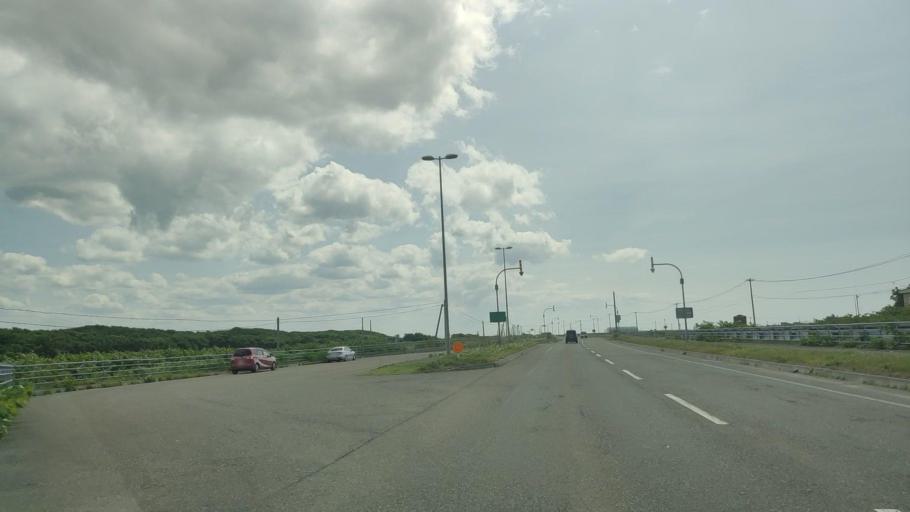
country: JP
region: Hokkaido
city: Makubetsu
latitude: 44.8717
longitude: 141.7519
